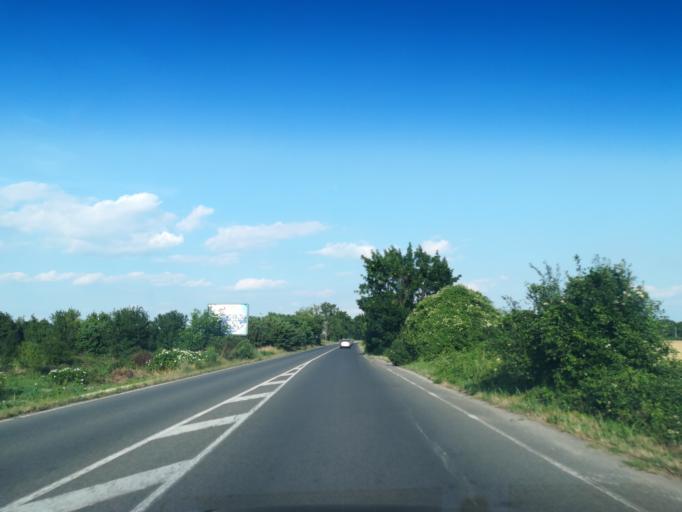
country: BG
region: Plovdiv
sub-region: Obshtina Plovdiv
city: Plovdiv
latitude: 42.1485
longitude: 24.8308
